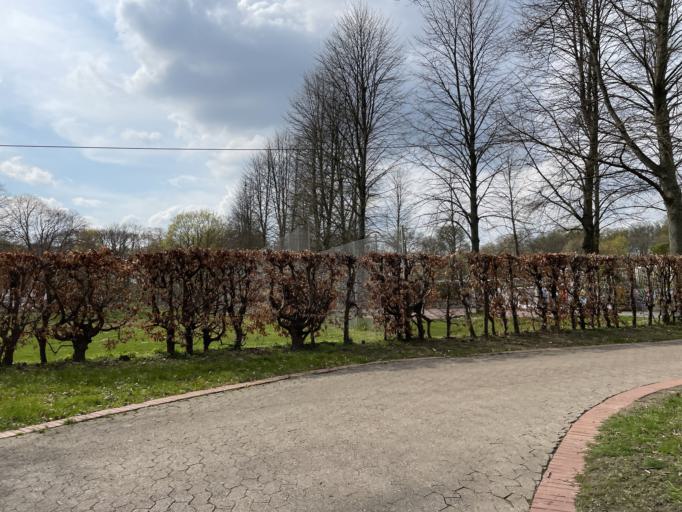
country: DE
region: North Rhine-Westphalia
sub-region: Regierungsbezirk Detmold
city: Minden
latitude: 52.2824
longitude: 8.9194
